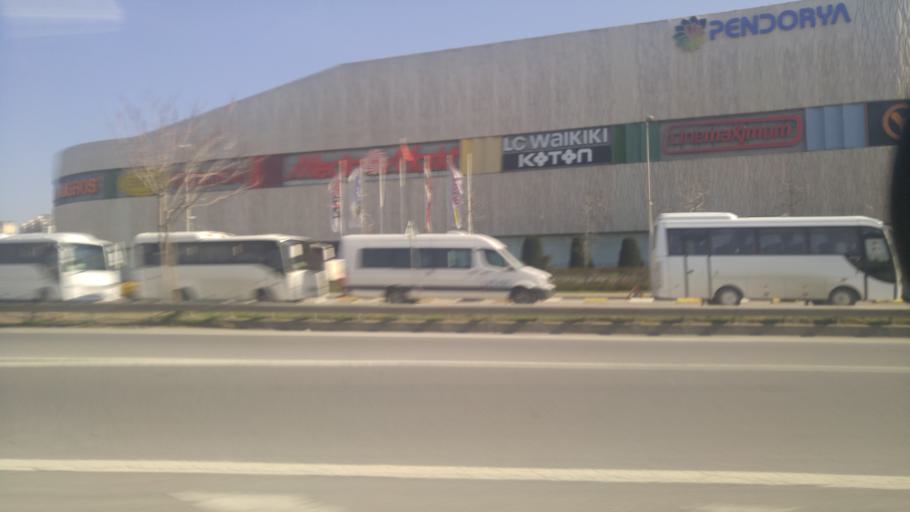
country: TR
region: Istanbul
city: Pendik
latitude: 40.8654
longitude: 29.2742
